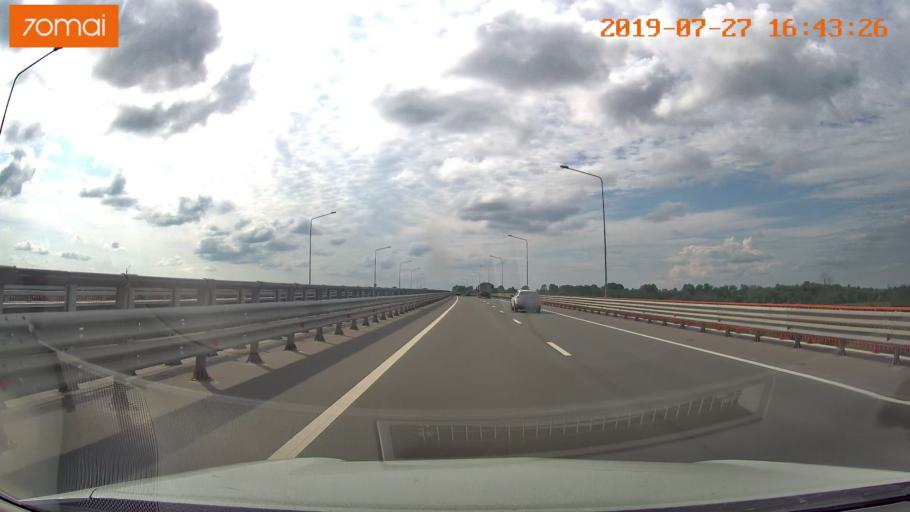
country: RU
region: Kaliningrad
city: Gvardeysk
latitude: 54.6711
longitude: 21.1028
